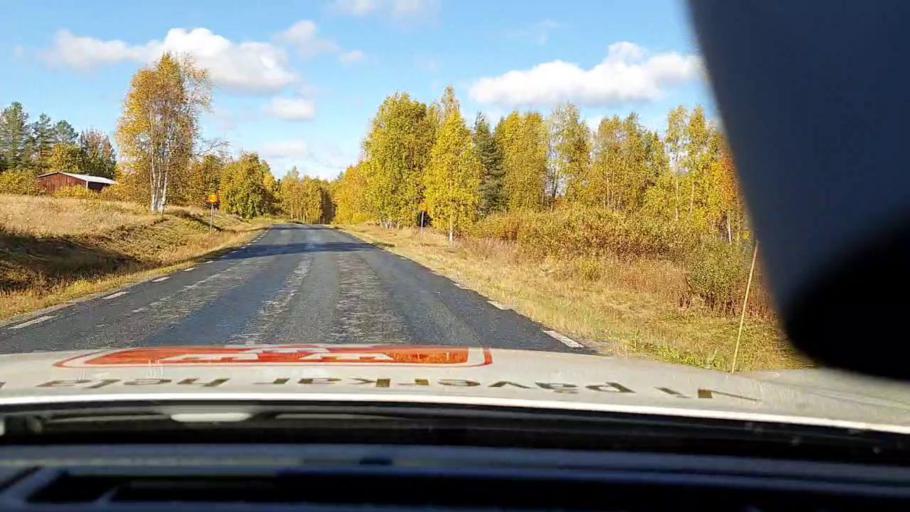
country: SE
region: Vaesterbotten
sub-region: Skelleftea Kommun
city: Langsele
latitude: 65.0051
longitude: 20.0906
